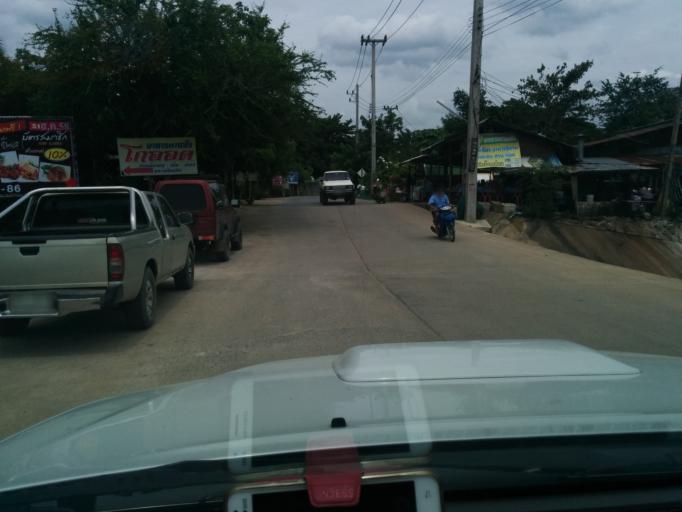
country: TH
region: Sara Buri
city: Muak Lek
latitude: 14.5815
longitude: 101.2308
